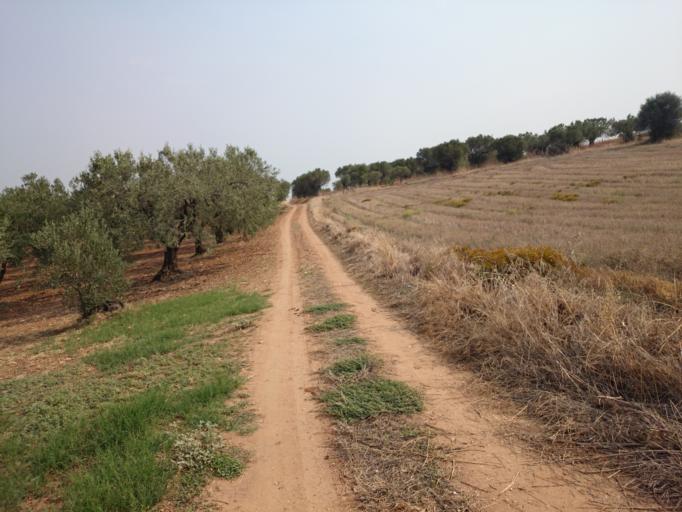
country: GR
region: Central Macedonia
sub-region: Nomos Chalkidikis
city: Nea Moudhania
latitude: 40.2546
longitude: 23.2700
